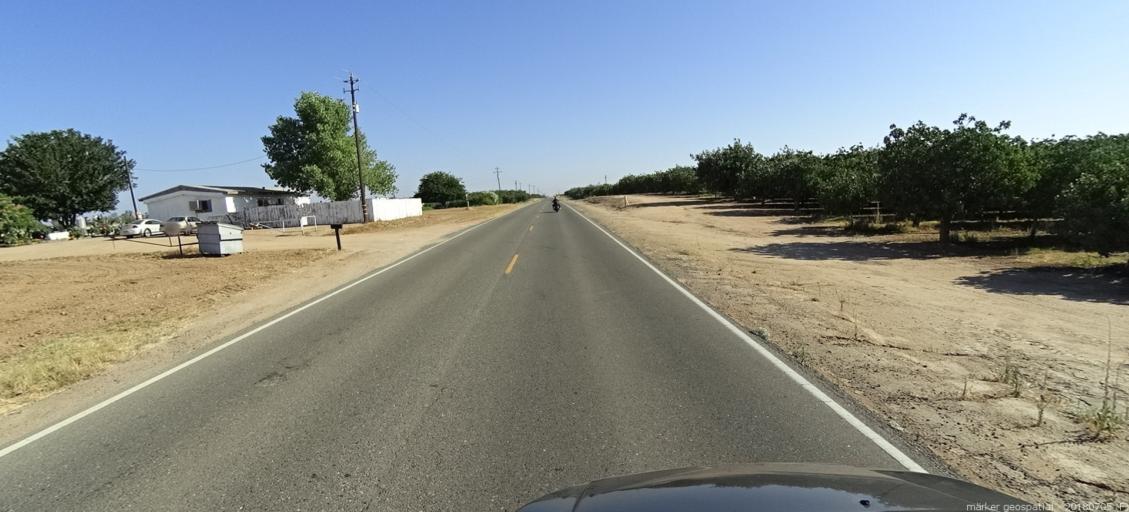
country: US
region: California
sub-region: Madera County
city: Madera Acres
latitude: 37.0488
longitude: -120.0745
